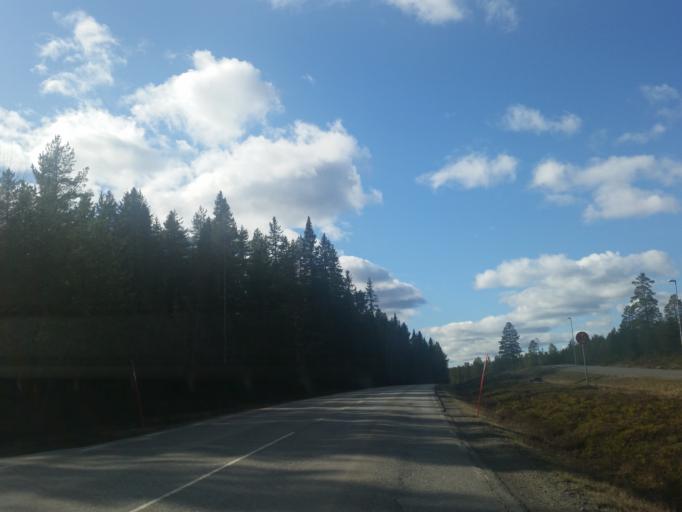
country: SE
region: Vaesterbotten
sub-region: Robertsfors Kommun
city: Robertsfors
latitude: 64.1773
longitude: 20.9026
